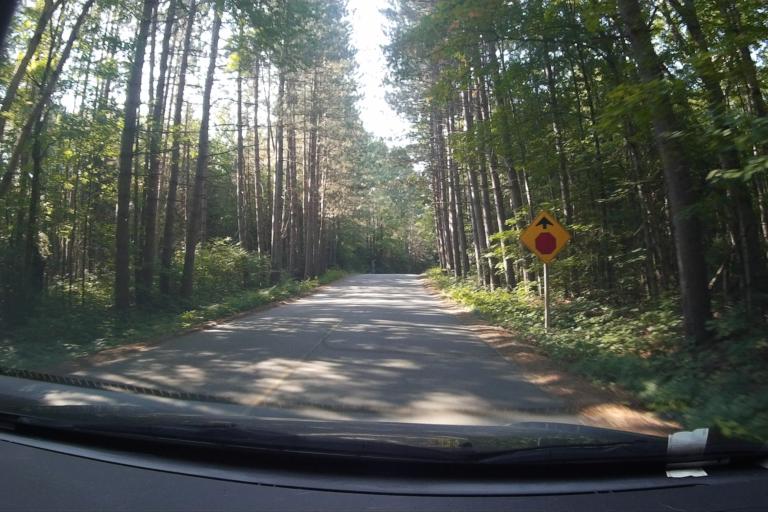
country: CA
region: Ontario
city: Huntsville
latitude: 45.5557
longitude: -78.6000
